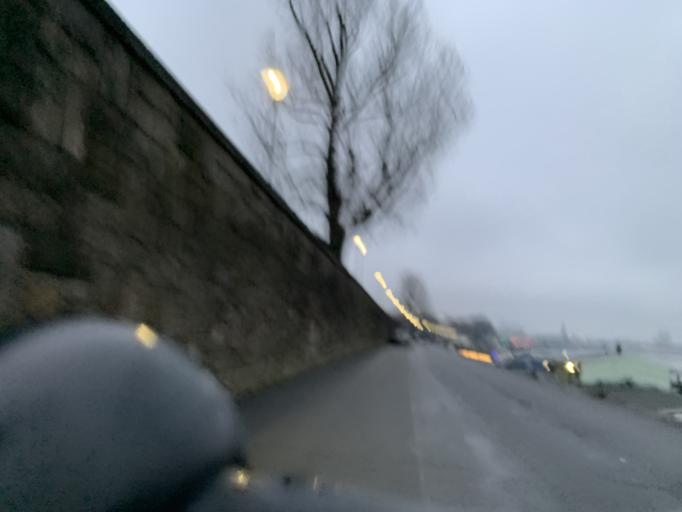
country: DE
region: North Rhine-Westphalia
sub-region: Regierungsbezirk Dusseldorf
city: Dusseldorf
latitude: 51.2413
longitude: 6.7680
